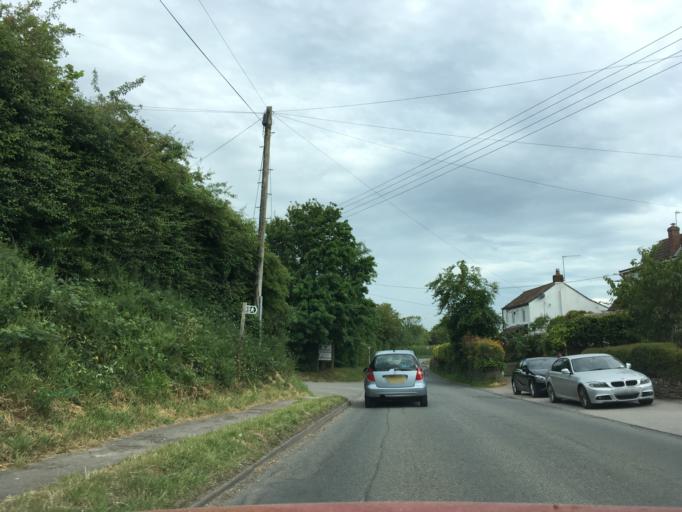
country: GB
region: England
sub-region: North Somerset
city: Portishead
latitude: 51.4642
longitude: -2.7583
